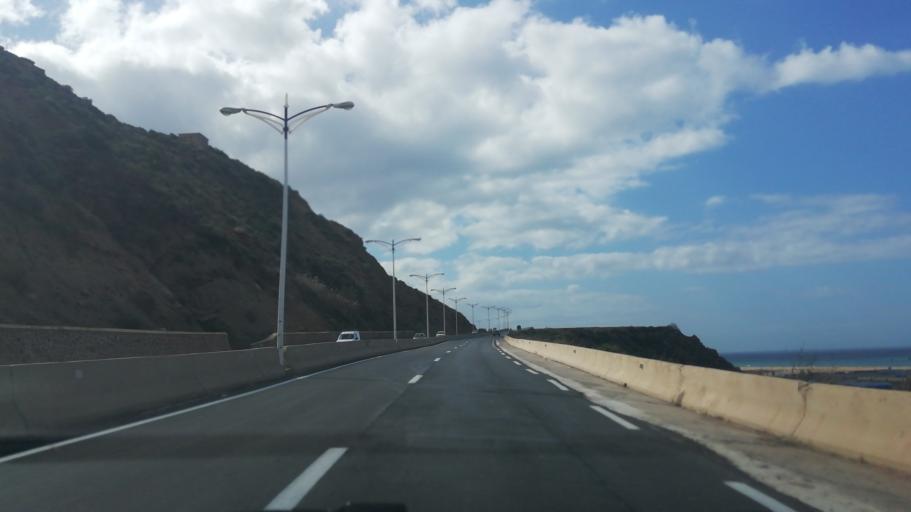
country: DZ
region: Mostaganem
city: Mostaganem
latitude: 36.0113
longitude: 0.1288
